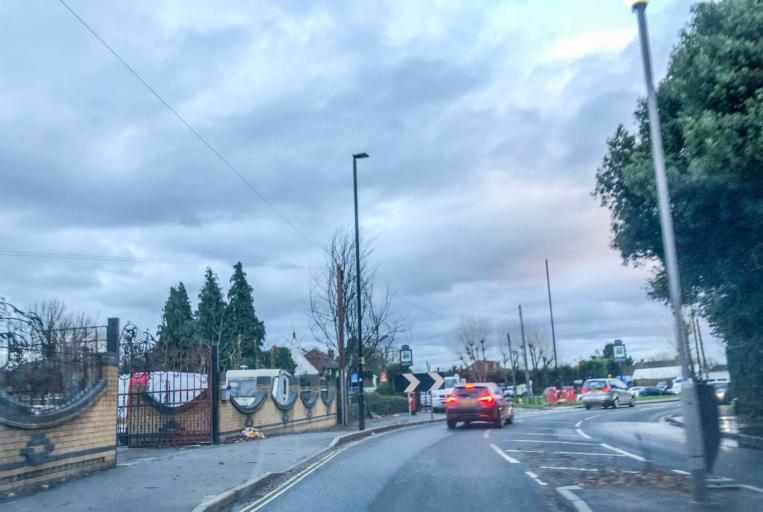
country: GB
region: England
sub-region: Greater London
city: Feltham
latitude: 51.4657
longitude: -0.4183
